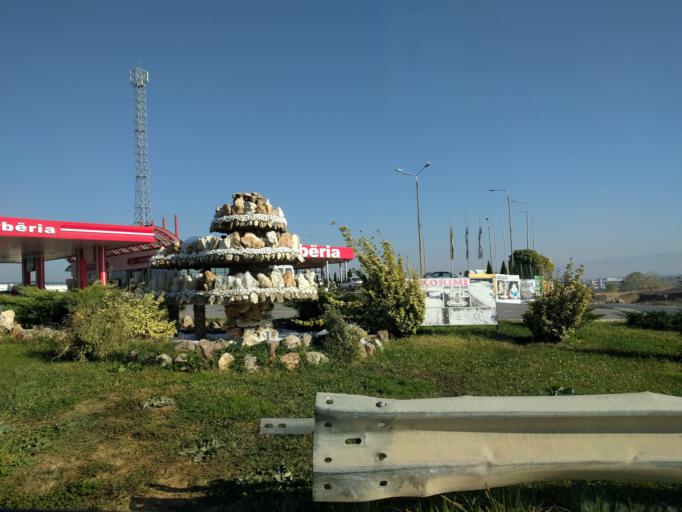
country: XK
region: Prizren
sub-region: Prizren
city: Prizren
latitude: 42.2475
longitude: 20.7207
